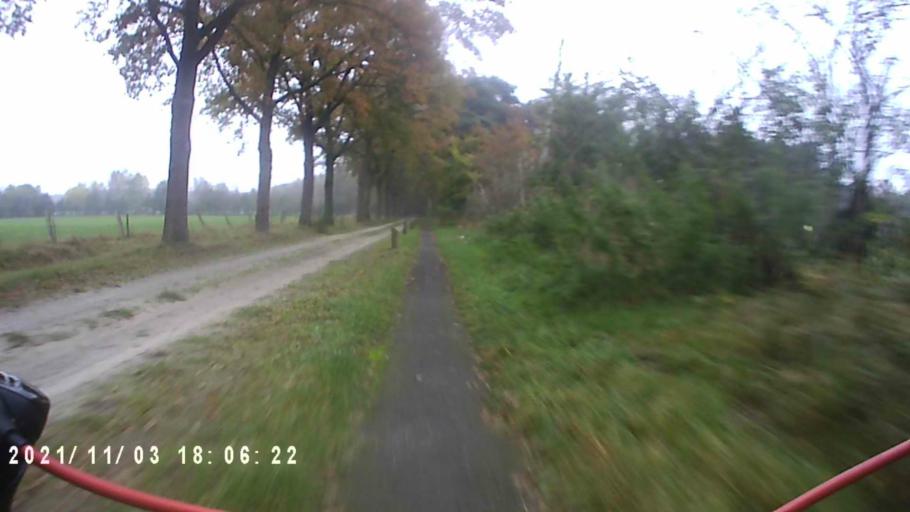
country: NL
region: Drenthe
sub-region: Gemeente Westerveld
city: Dwingeloo
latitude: 52.8201
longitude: 6.3590
